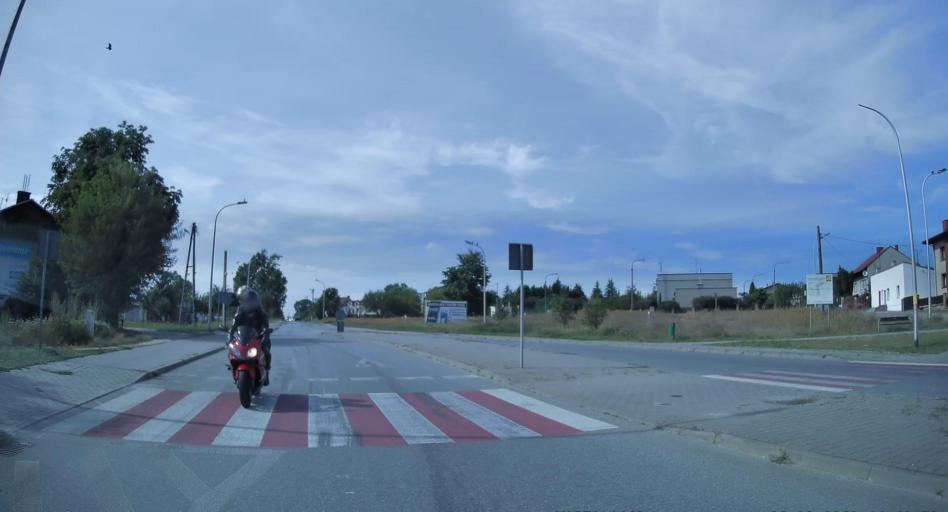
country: PL
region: Lodz Voivodeship
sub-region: Powiat tomaszowski
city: Tomaszow Mazowiecki
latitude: 51.5397
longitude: 20.0006
